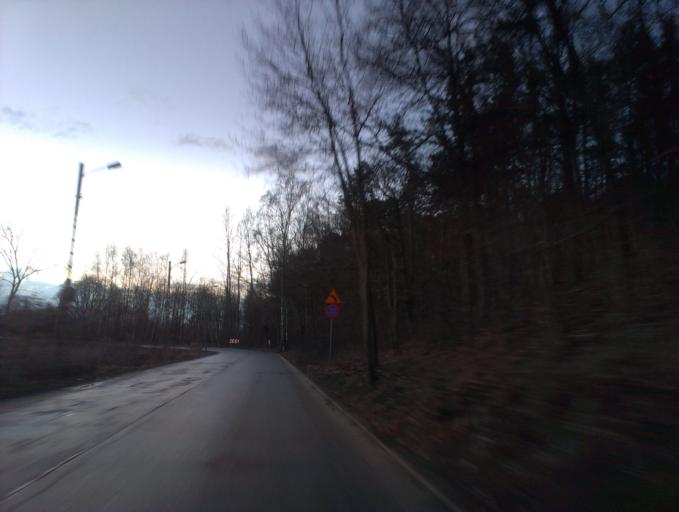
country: PL
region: Masovian Voivodeship
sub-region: Warszawa
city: Kabaty
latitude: 52.1210
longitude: 21.0907
